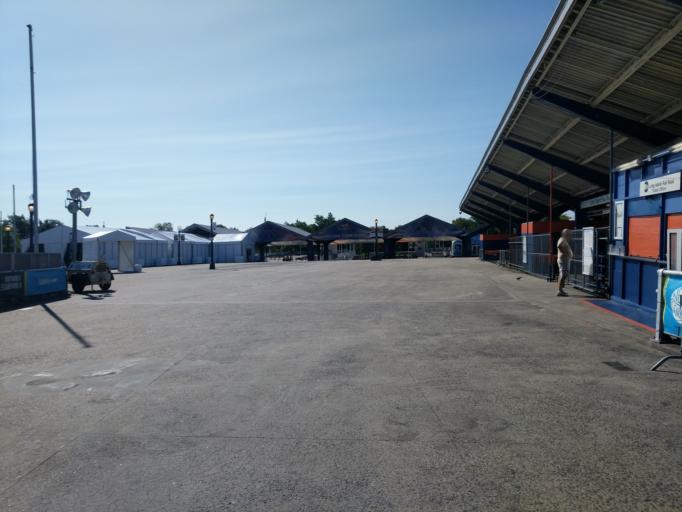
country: US
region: New York
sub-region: Queens County
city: Borough of Queens
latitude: 40.7526
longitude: -73.8440
